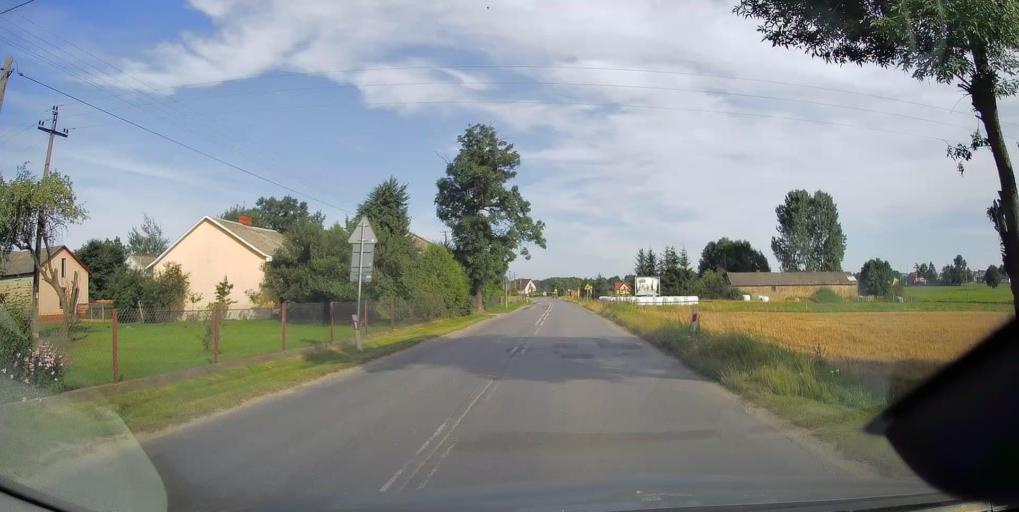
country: PL
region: Swietokrzyskie
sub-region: Powiat kielecki
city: Lopuszno
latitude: 50.9720
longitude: 20.2419
